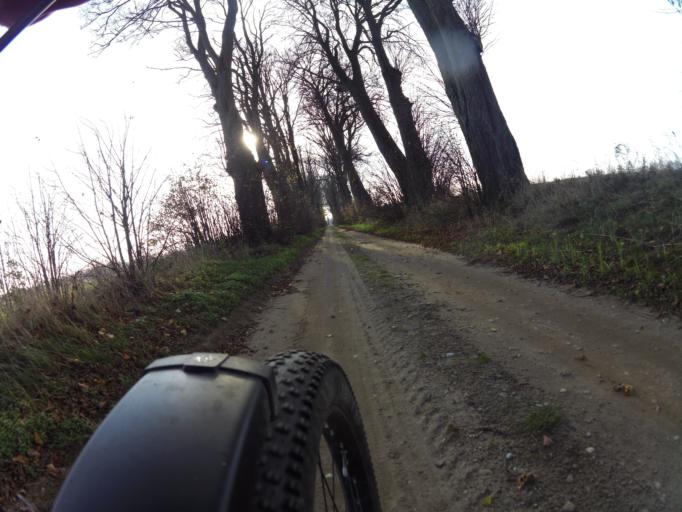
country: PL
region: Pomeranian Voivodeship
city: Strzelno
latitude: 54.7522
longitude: 18.2903
